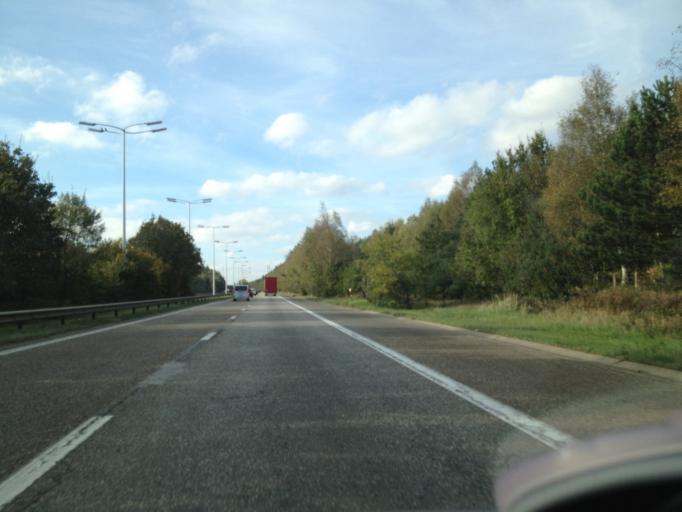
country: BE
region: Flanders
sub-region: Provincie Limburg
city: Maasmechelen
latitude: 50.9575
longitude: 5.6565
